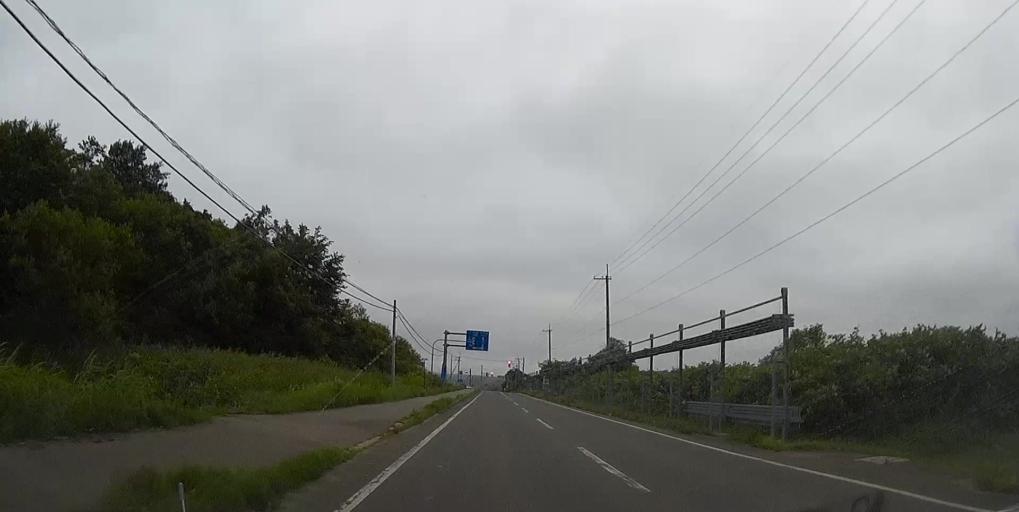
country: JP
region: Hokkaido
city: Iwanai
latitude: 42.4125
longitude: 140.0047
